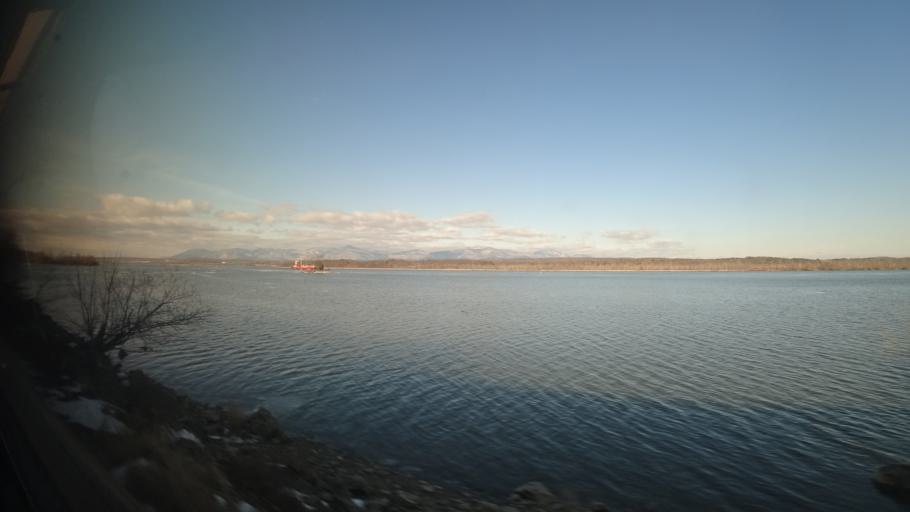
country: US
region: New York
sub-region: Greene County
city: Catskill
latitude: 42.1848
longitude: -73.8553
